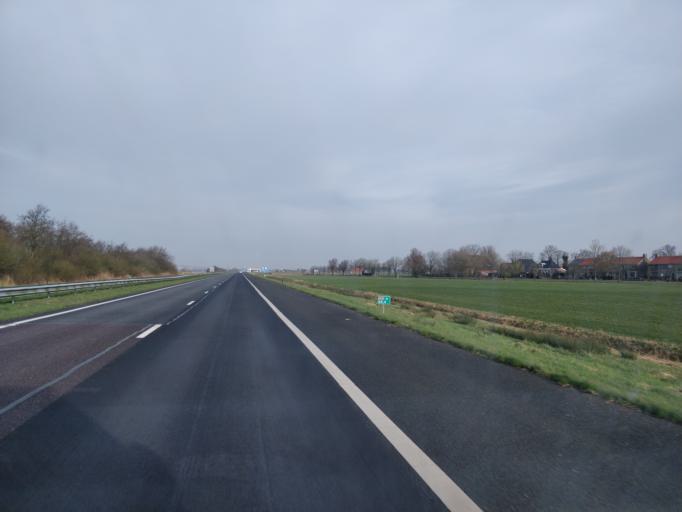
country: NL
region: Friesland
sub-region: Gemeente Boarnsterhim
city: Reduzum
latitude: 53.1194
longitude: 5.8088
